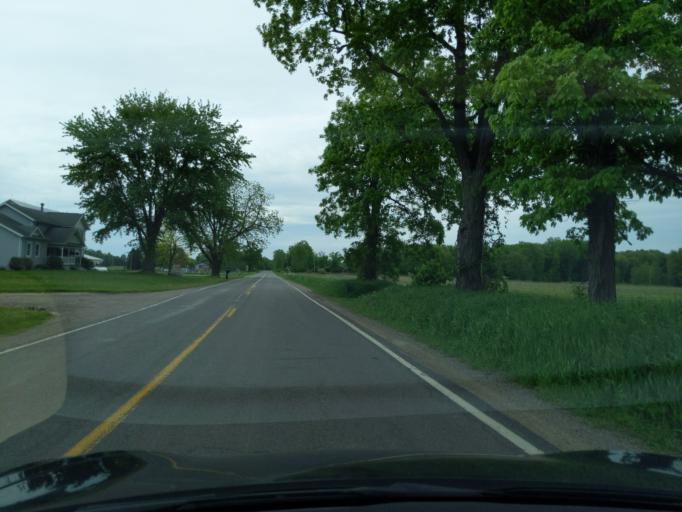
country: US
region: Michigan
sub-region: Ingham County
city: Leslie
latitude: 42.4578
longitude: -84.3512
